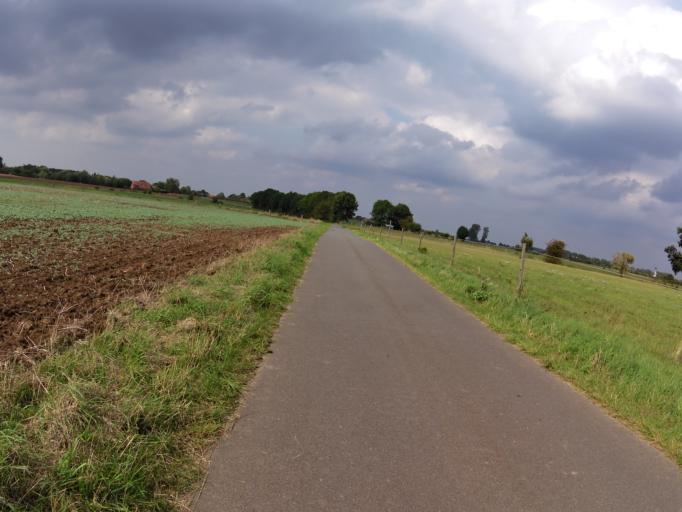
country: DE
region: Lower Saxony
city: Blender
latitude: 52.9066
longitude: 9.1650
